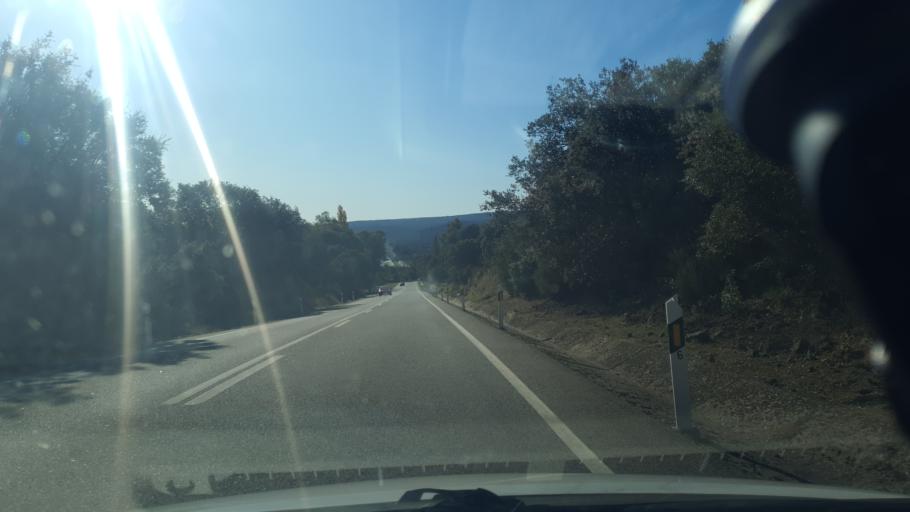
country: ES
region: Castille and Leon
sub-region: Provincia de Avila
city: Arenas de San Pedro
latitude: 40.1934
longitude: -5.0468
